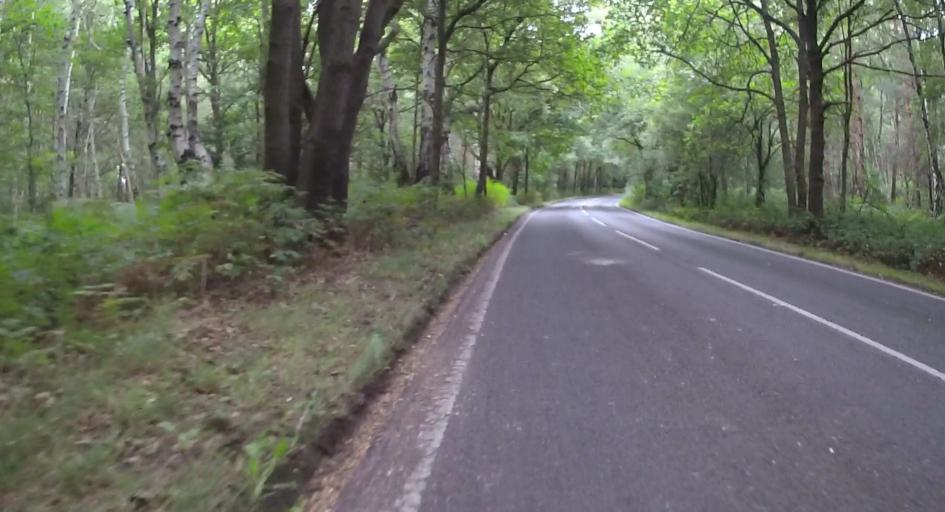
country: GB
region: England
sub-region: Surrey
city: West Byfleet
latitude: 51.3220
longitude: -0.5228
